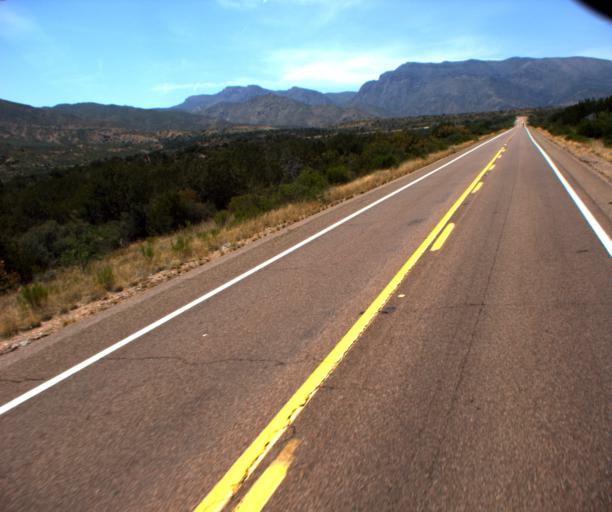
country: US
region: Arizona
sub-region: Gila County
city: Payson
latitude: 34.0305
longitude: -111.3534
